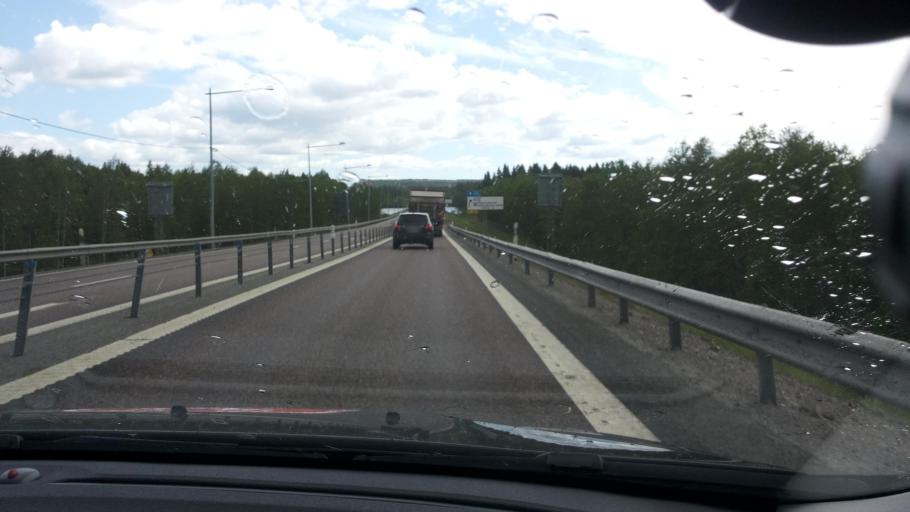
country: SE
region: Vaesternorrland
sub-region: Timra Kommun
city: Bergeforsen
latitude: 62.5173
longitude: 17.4141
